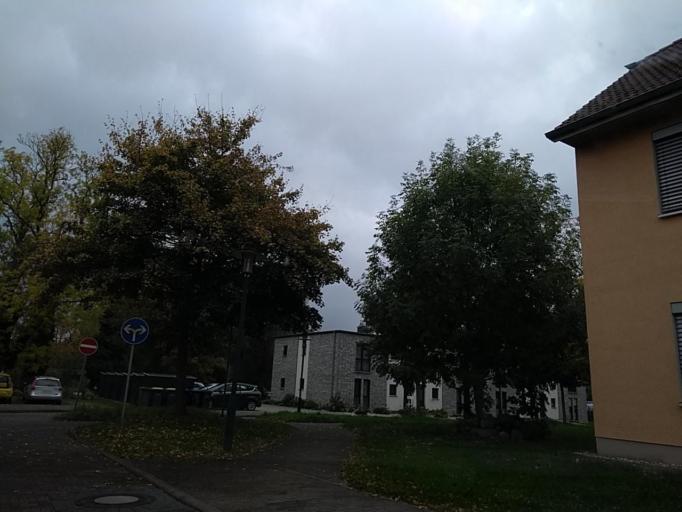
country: DE
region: Mecklenburg-Vorpommern
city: Bad Doberan
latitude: 54.1100
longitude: 11.9072
